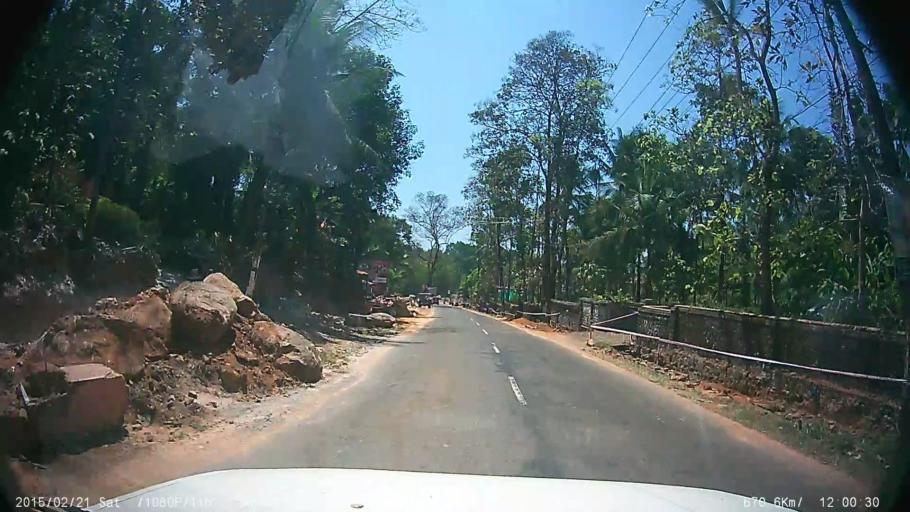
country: IN
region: Kerala
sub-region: Kottayam
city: Lalam
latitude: 9.7284
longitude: 76.6934
